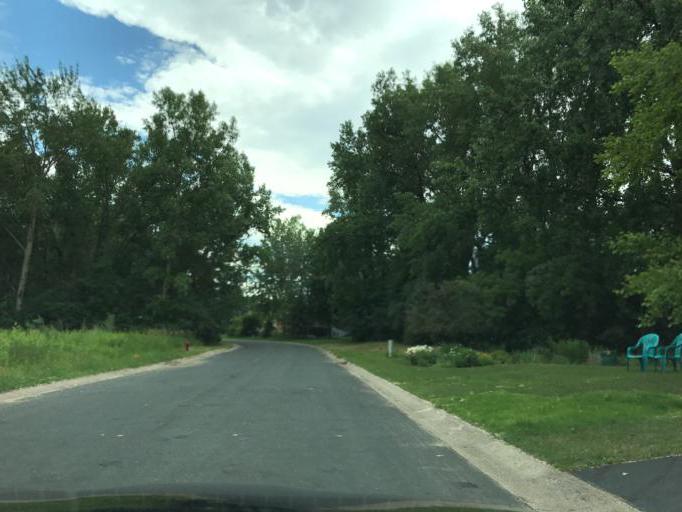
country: US
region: Minnesota
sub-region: Hennepin County
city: Osseo
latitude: 45.0837
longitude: -93.4127
